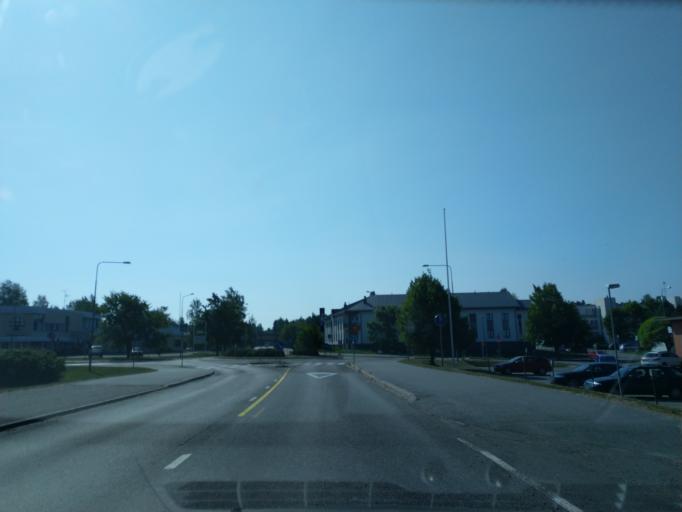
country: FI
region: Satakunta
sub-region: Pori
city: Noormarkku
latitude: 61.5933
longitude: 21.8678
